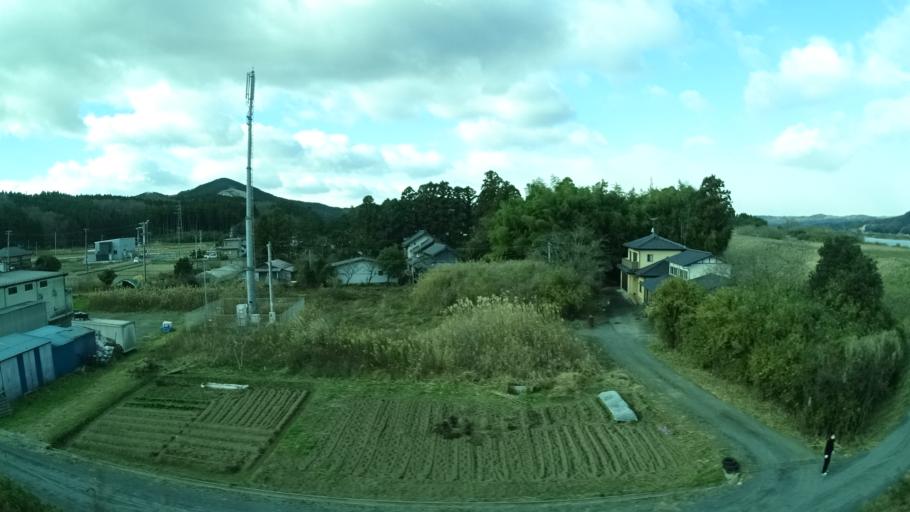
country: JP
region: Miyagi
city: Iwanuma
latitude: 38.0759
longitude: 140.8536
